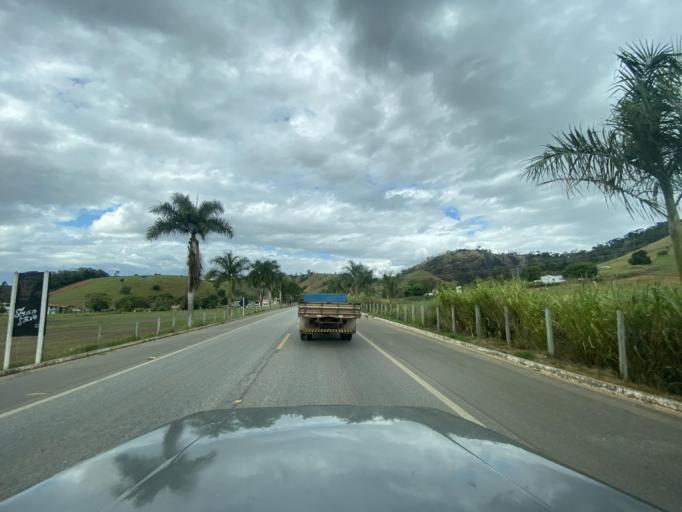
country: BR
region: Espirito Santo
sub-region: Jeronimo Monteiro
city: Jeronimo Monteiro
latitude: -20.7621
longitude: -41.4535
